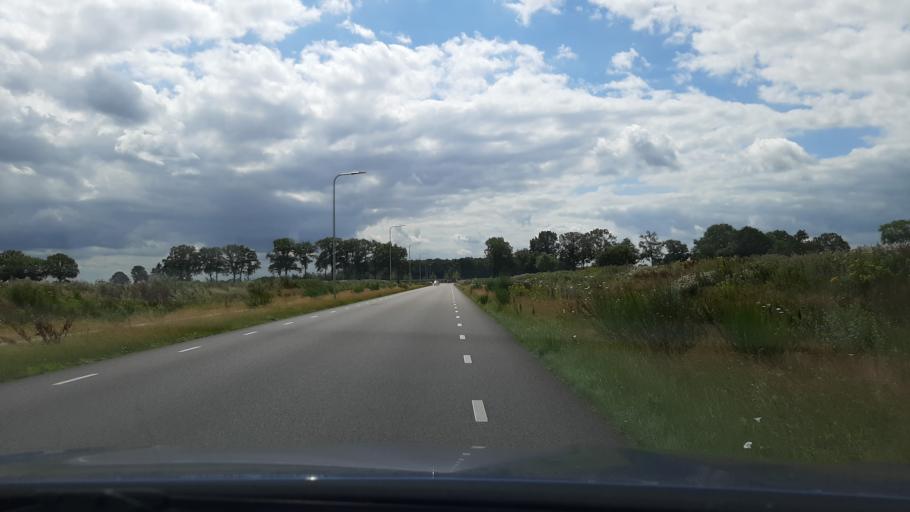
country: NL
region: Drenthe
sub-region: Gemeente Hoogeveen
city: Hoogeveen
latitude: 52.7041
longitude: 6.5167
